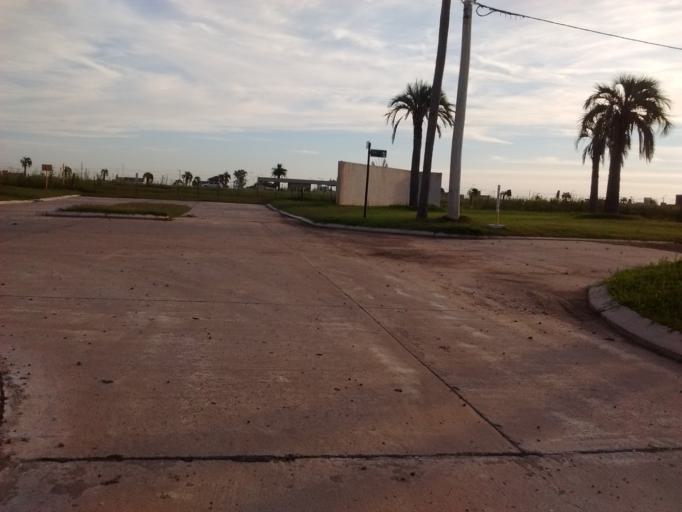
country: AR
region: Santa Fe
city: Roldan
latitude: -32.9291
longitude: -60.8748
